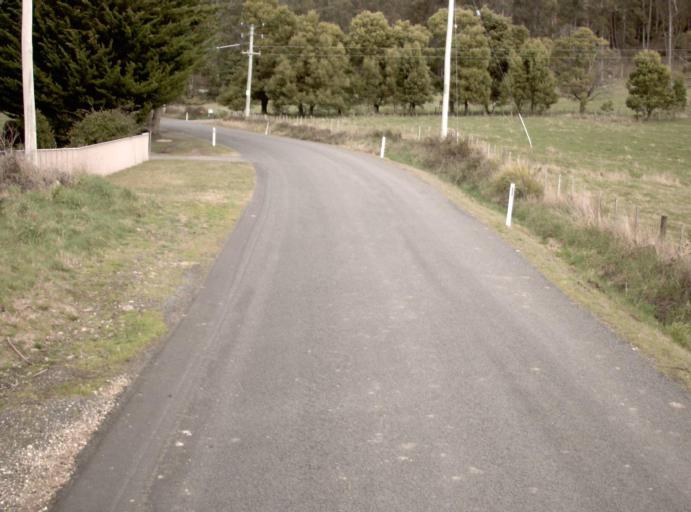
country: AU
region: Tasmania
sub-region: Launceston
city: Mayfield
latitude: -41.2660
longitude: 147.1605
